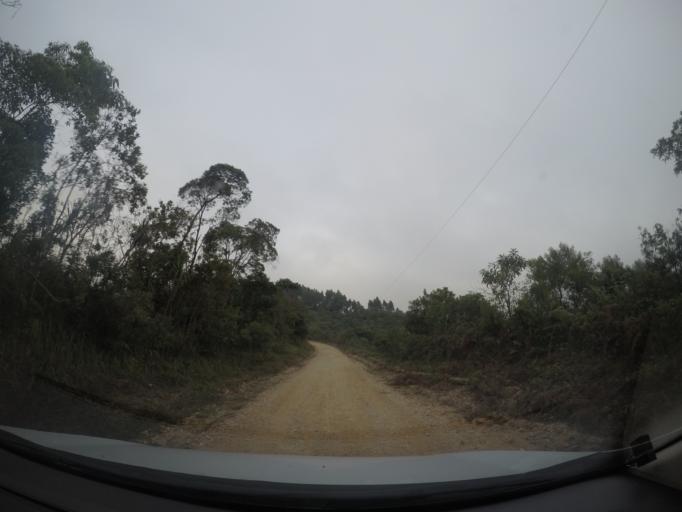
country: BR
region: Parana
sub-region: Colombo
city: Colombo
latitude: -25.3138
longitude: -49.2462
